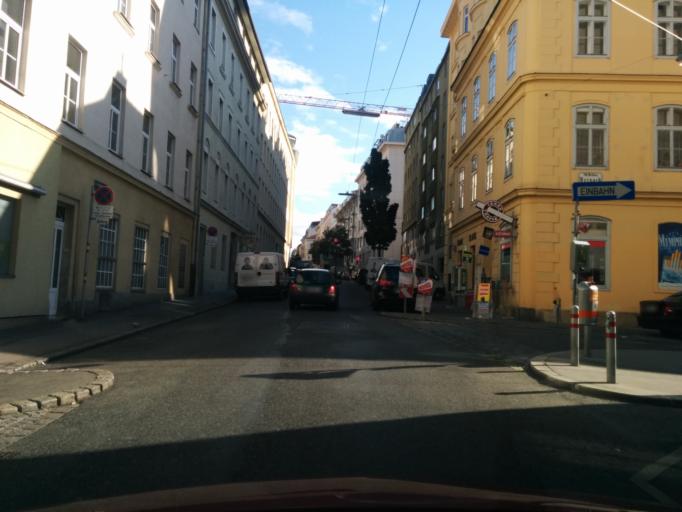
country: AT
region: Vienna
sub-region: Wien Stadt
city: Vienna
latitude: 48.2067
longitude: 16.3434
